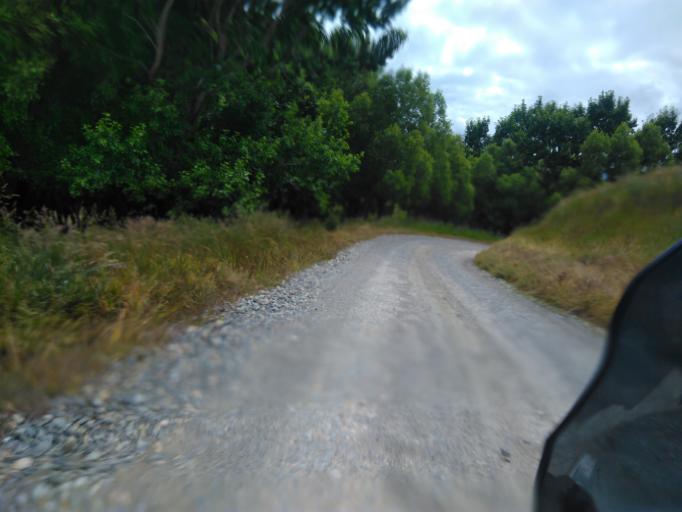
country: NZ
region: Gisborne
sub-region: Gisborne District
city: Gisborne
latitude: -38.1891
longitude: 178.1006
